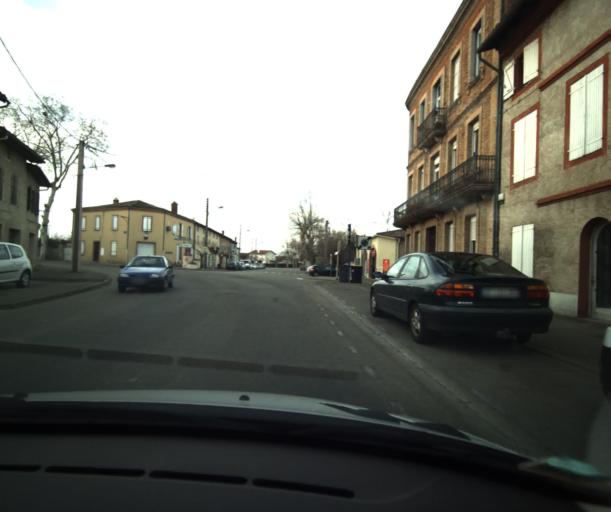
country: FR
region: Midi-Pyrenees
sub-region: Departement du Tarn-et-Garonne
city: Montech
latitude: 43.9563
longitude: 1.2282
